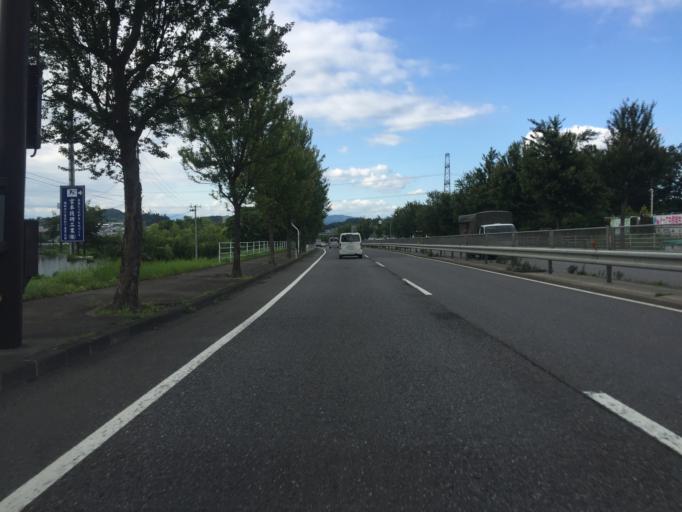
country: JP
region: Fukushima
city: Nihommatsu
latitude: 37.6434
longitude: 140.4861
